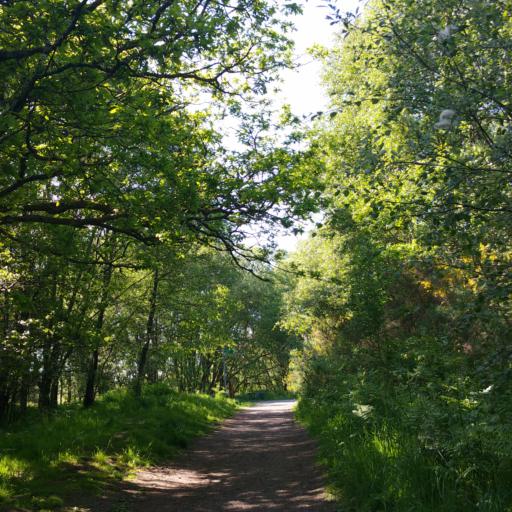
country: GB
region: Scotland
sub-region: East Dunbartonshire
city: Milngavie
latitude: 55.9550
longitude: -4.3270
